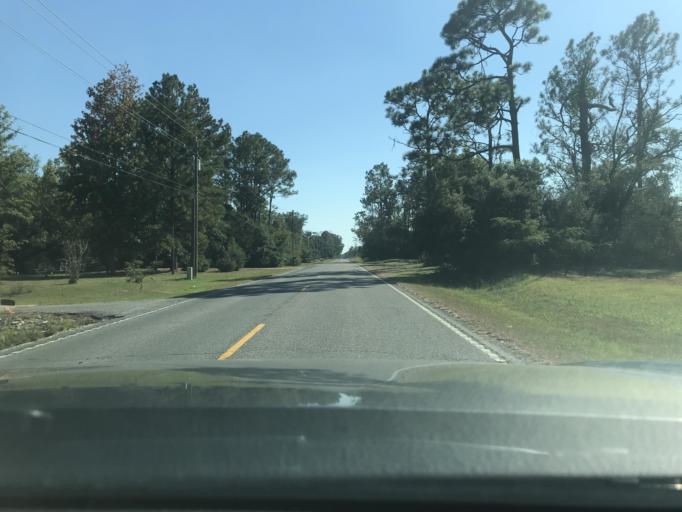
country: US
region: Louisiana
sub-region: Calcasieu Parish
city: Moss Bluff
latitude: 30.3265
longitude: -93.2582
